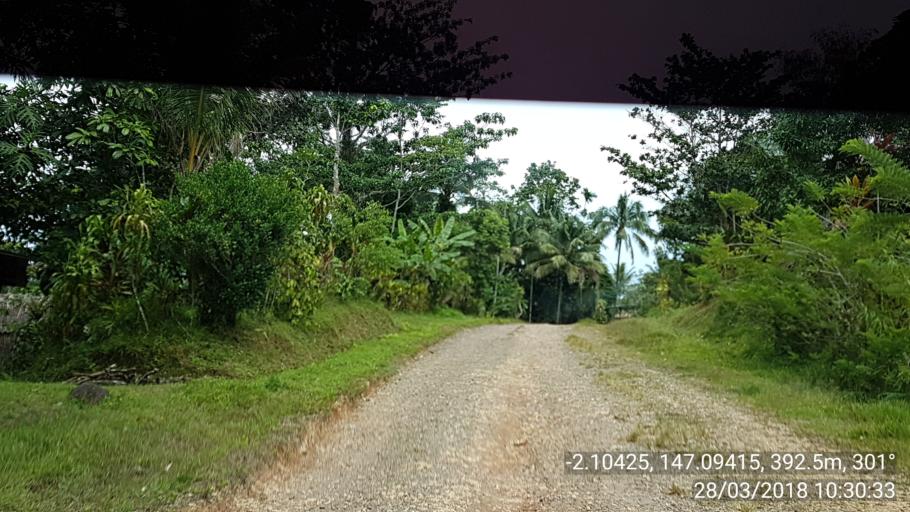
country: PG
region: Manus
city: Lorengau
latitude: -2.1041
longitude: 147.0942
